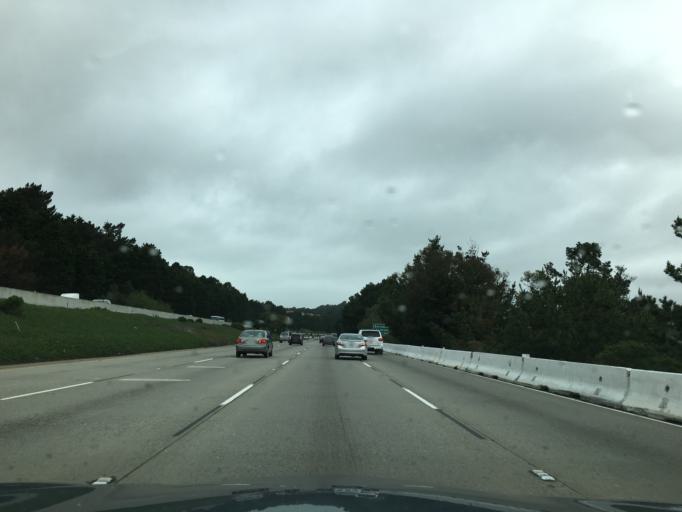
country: US
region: California
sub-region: San Mateo County
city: Colma
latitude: 37.6570
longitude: -122.4598
